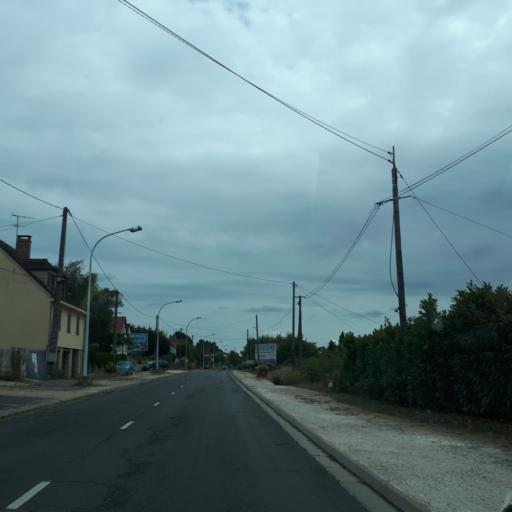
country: FR
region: Centre
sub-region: Departement du Loiret
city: Poilly-lez-Gien
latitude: 47.6986
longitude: 2.6063
